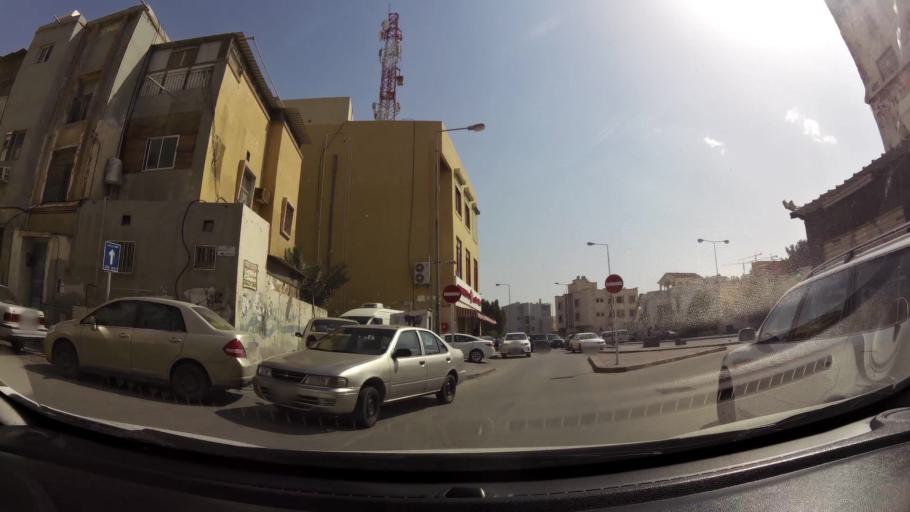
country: BH
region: Manama
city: Jidd Hafs
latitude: 26.2098
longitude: 50.4572
